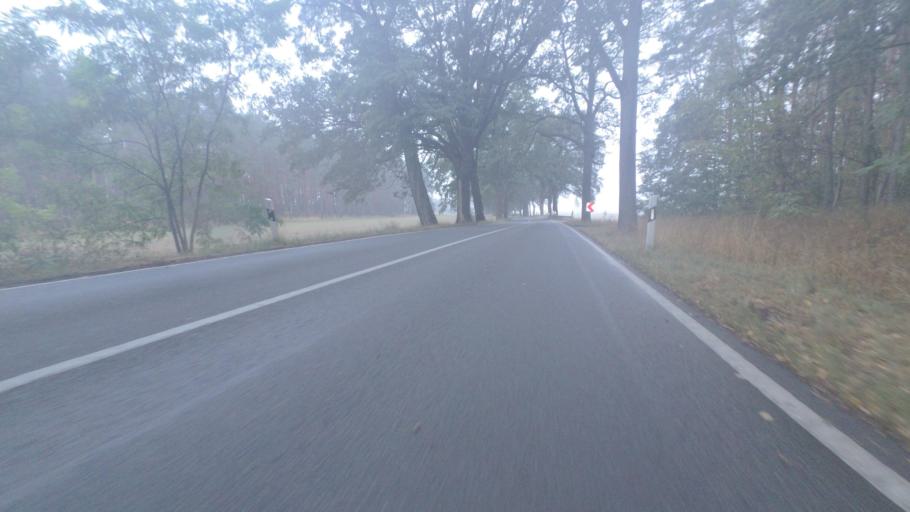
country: DE
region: Brandenburg
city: Heiligengrabe
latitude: 53.0944
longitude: 12.3619
